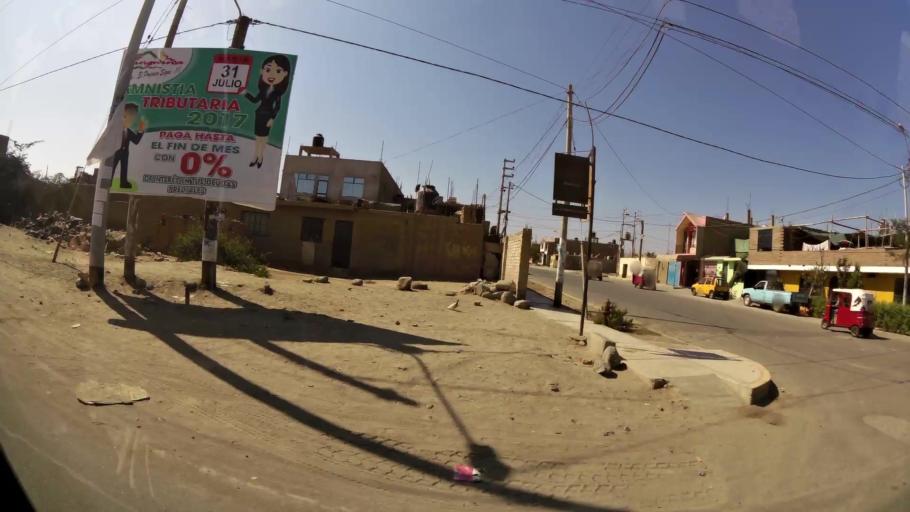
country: PE
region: Ica
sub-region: Provincia de Ica
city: La Tinguina
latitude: -14.0319
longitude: -75.7095
